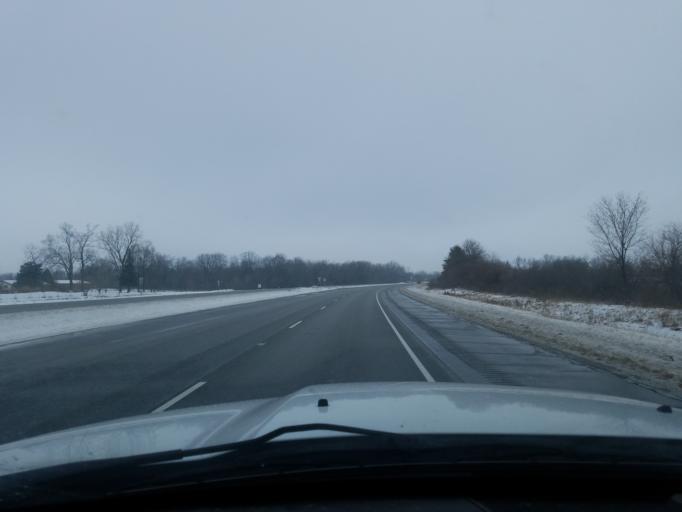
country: US
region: Indiana
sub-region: Fulton County
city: Rochester
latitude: 40.9319
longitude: -86.1675
